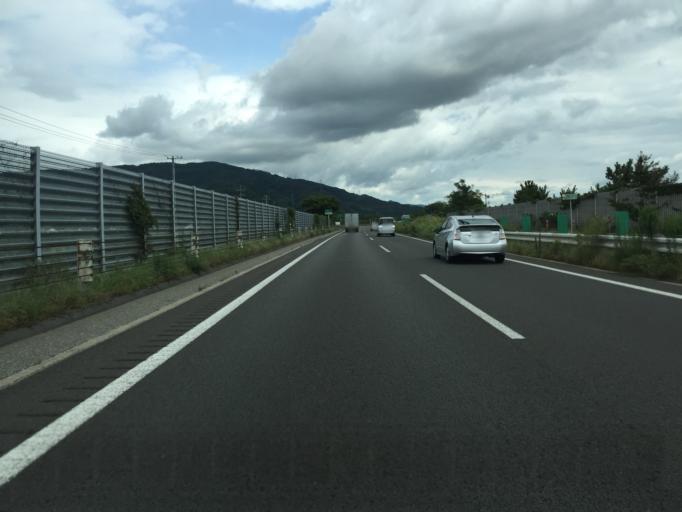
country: JP
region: Fukushima
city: Fukushima-shi
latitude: 37.8184
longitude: 140.4734
